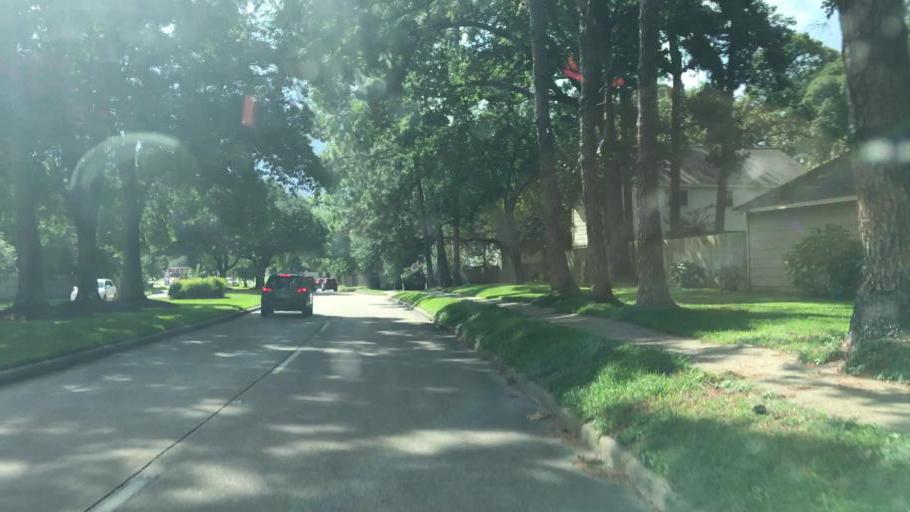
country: US
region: Texas
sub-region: Harris County
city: Atascocita
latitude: 30.0071
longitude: -95.1673
